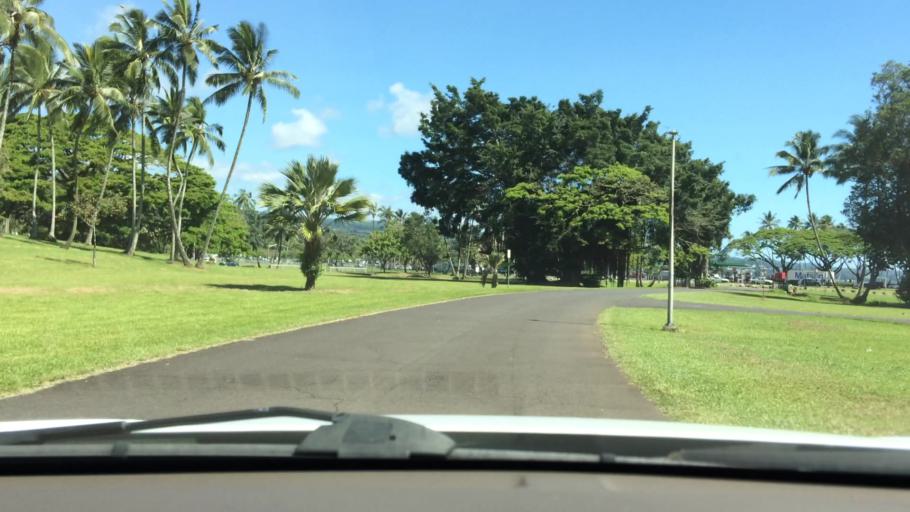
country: US
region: Hawaii
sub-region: Hawaii County
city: Hilo
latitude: 19.7199
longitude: -155.0775
